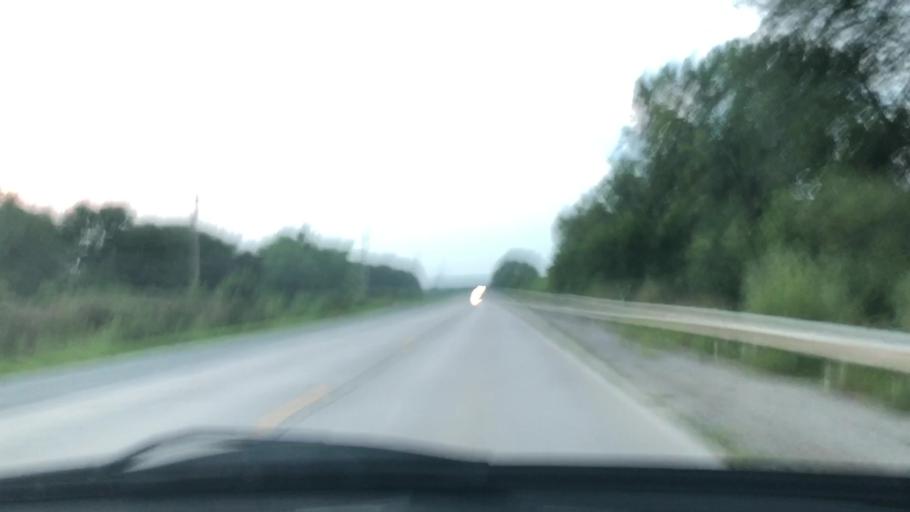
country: US
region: Iowa
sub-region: Johnson County
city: North Liberty
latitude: 41.7901
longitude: -91.6385
